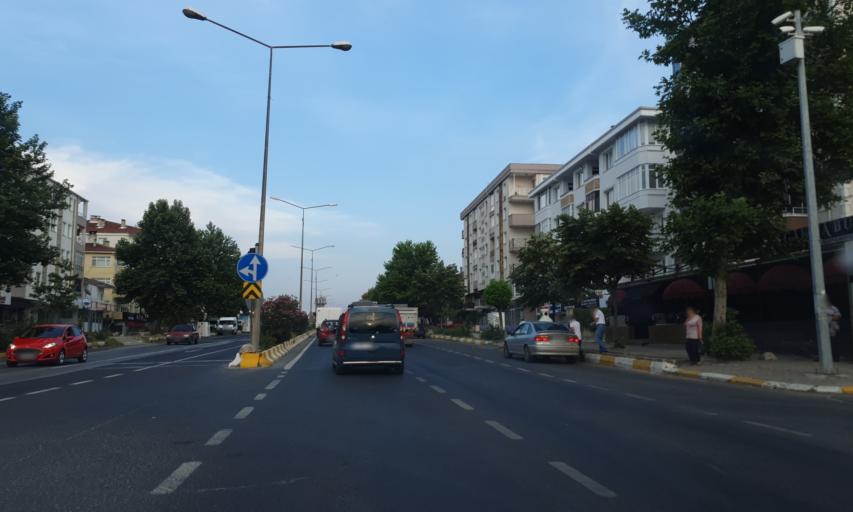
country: TR
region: Kirklareli
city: Luleburgaz
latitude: 41.4011
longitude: 27.3711
